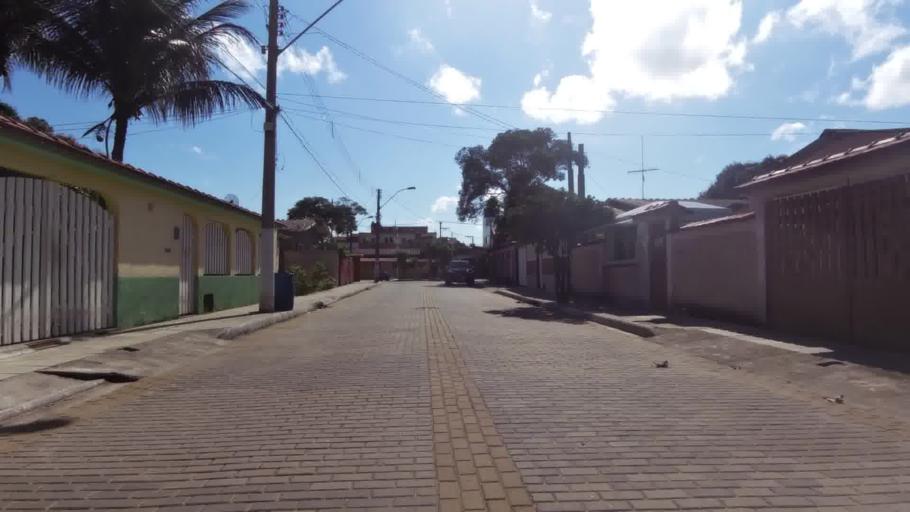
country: BR
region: Espirito Santo
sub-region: Piuma
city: Piuma
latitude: -20.8116
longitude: -40.6365
